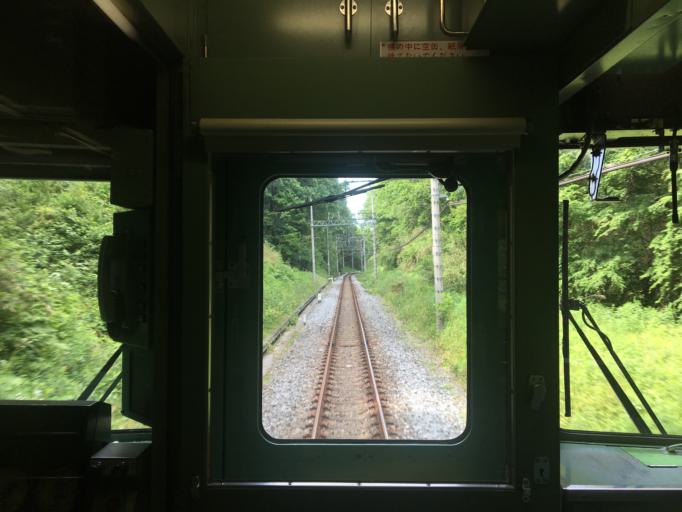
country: JP
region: Saitama
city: Ogawa
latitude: 36.0863
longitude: 139.2355
